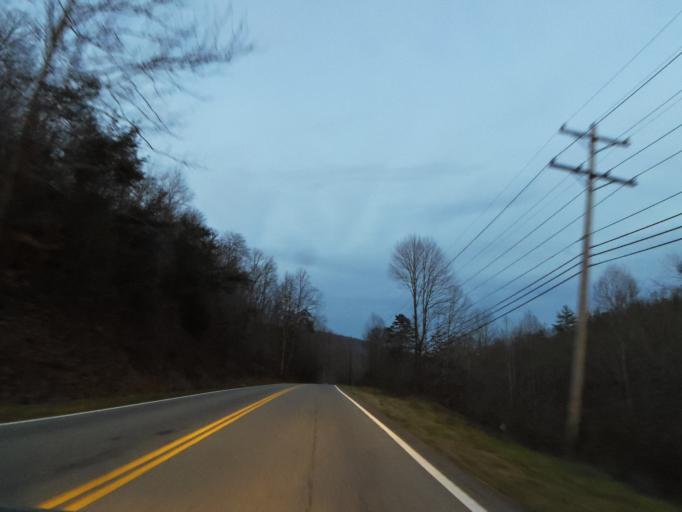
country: US
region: Tennessee
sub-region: Morgan County
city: Coalfield
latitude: 35.9721
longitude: -84.4630
